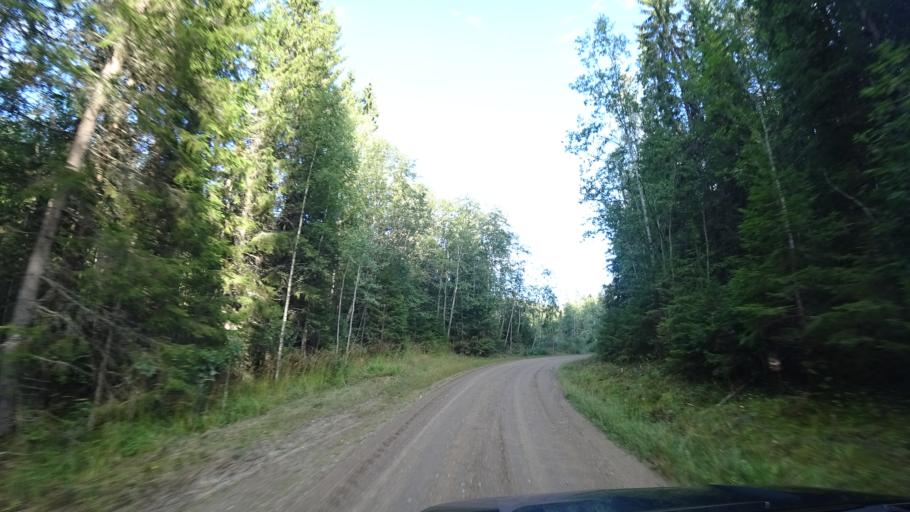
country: FI
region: Paijanne Tavastia
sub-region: Lahti
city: Auttoinen
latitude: 61.2188
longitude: 25.2101
